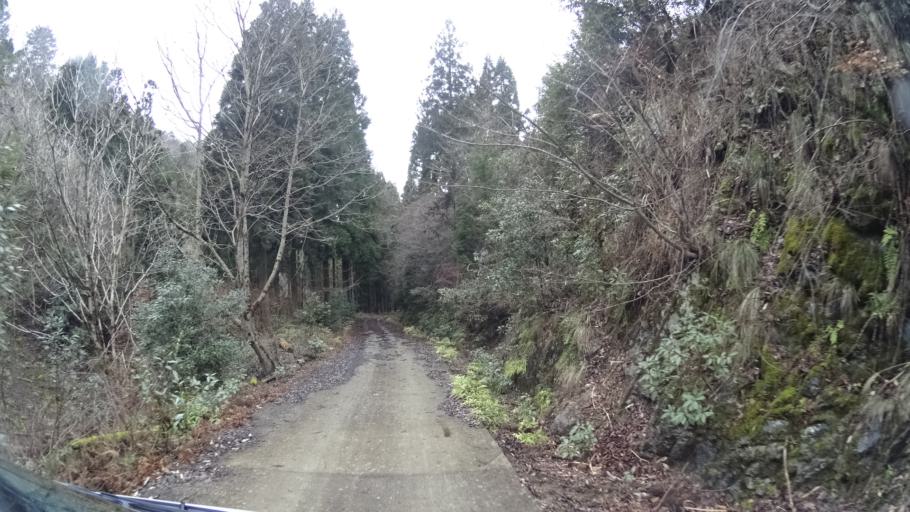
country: JP
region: Kyoto
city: Ayabe
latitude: 35.3119
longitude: 135.3743
